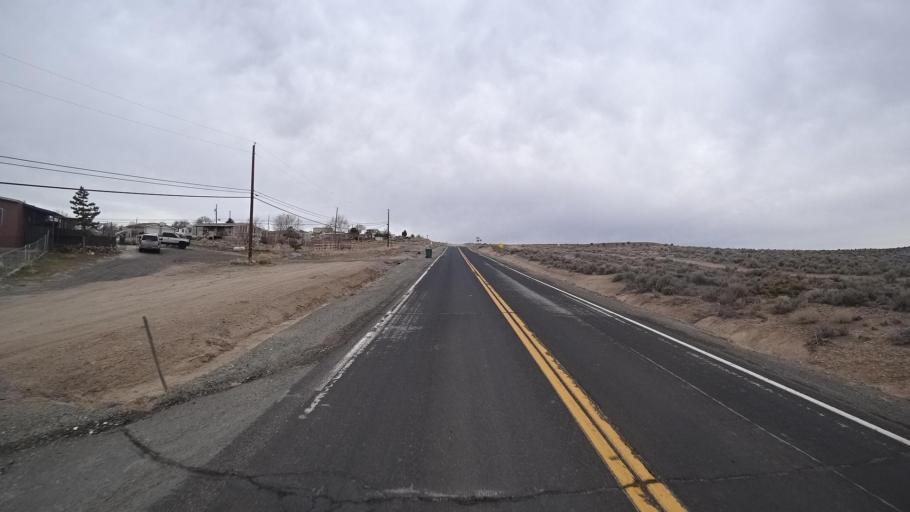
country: US
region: Nevada
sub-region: Washoe County
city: Lemmon Valley
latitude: 39.6754
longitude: -119.8524
